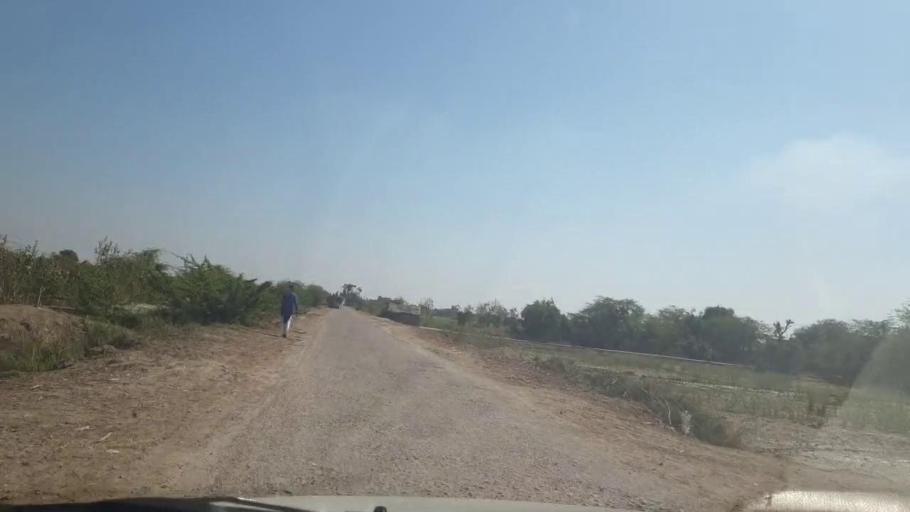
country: PK
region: Sindh
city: Mirpur Khas
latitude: 25.4863
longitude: 69.1694
